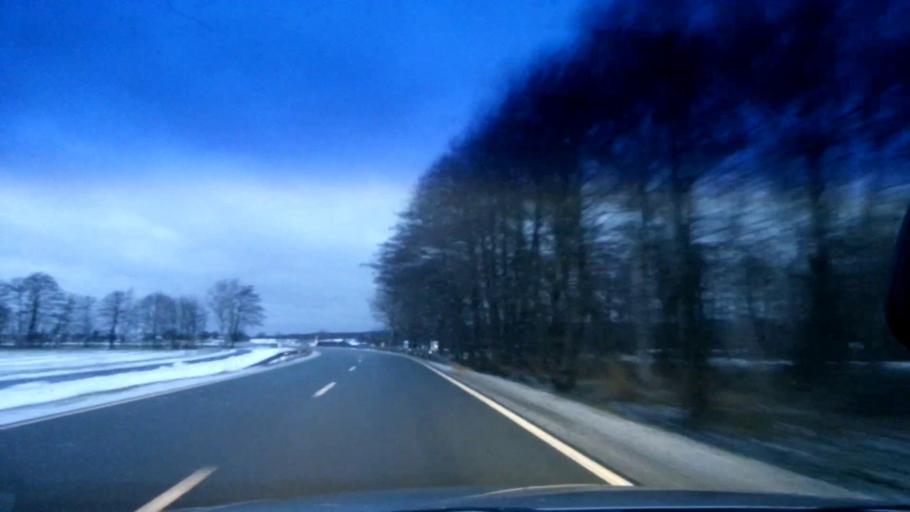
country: DE
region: Bavaria
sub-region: Upper Franconia
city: Weissenstadt
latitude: 50.0945
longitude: 11.8624
